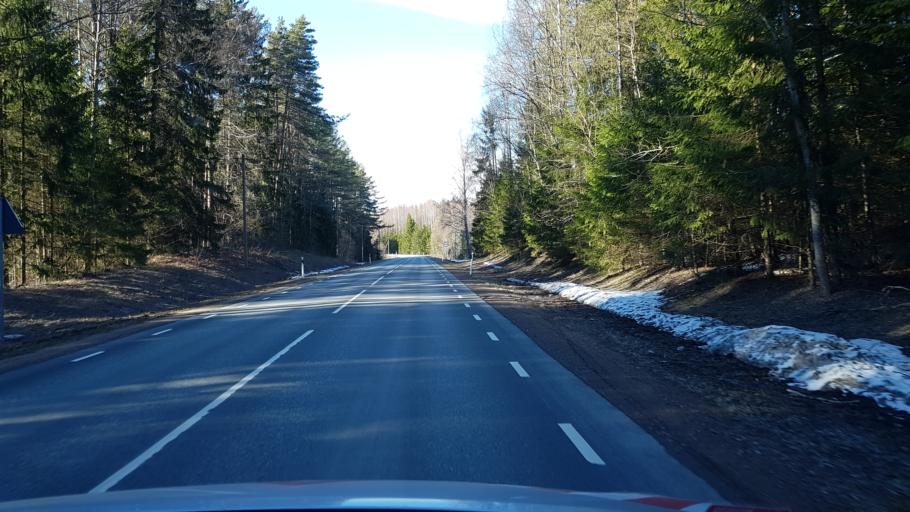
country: EE
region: Laeaene-Virumaa
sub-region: Kadrina vald
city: Kadrina
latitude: 59.3967
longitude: 26.0133
